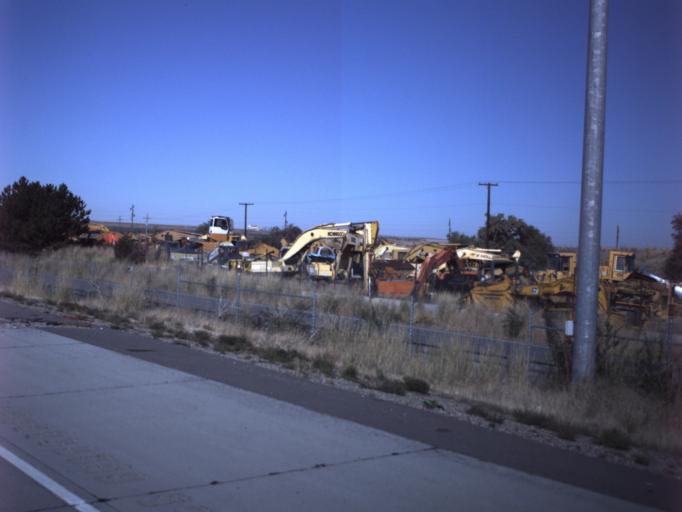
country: US
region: Utah
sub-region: Salt Lake County
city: West Valley City
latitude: 40.7253
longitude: -112.0391
